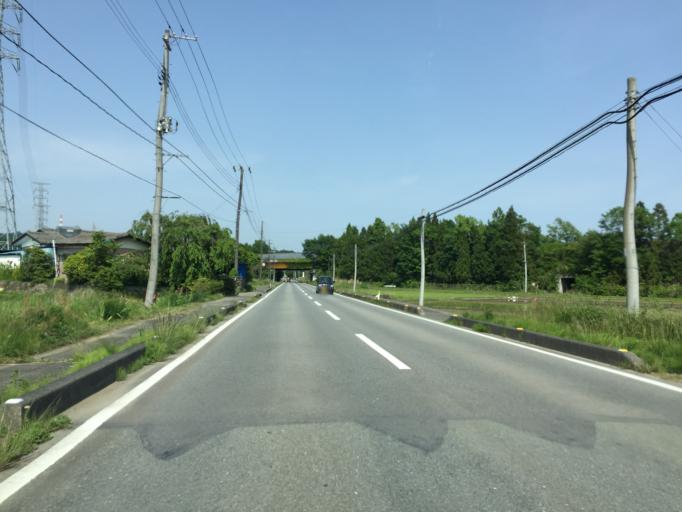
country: JP
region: Ibaraki
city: Kitaibaraki
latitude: 36.9261
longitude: 140.7603
